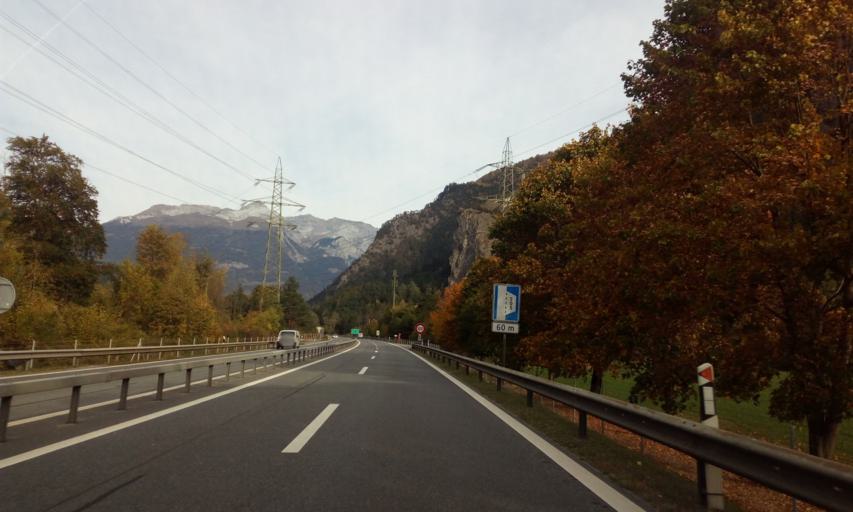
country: CH
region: Grisons
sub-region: Imboden District
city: Rhazuns
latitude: 46.7707
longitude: 9.4212
